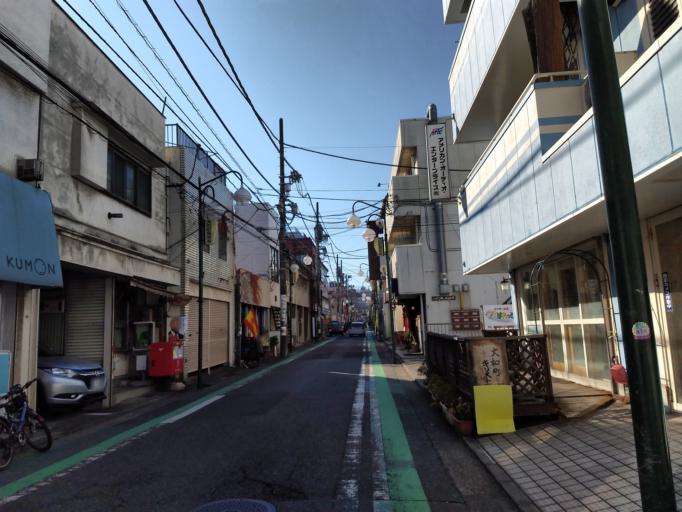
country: JP
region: Kanagawa
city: Yokohama
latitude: 35.4311
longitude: 139.6484
